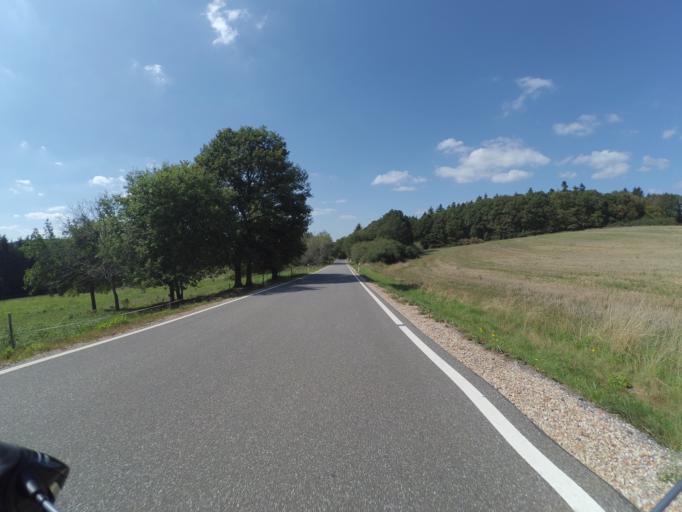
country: DE
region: Rheinland-Pfalz
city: Heidenburg
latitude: 49.8019
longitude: 6.9099
